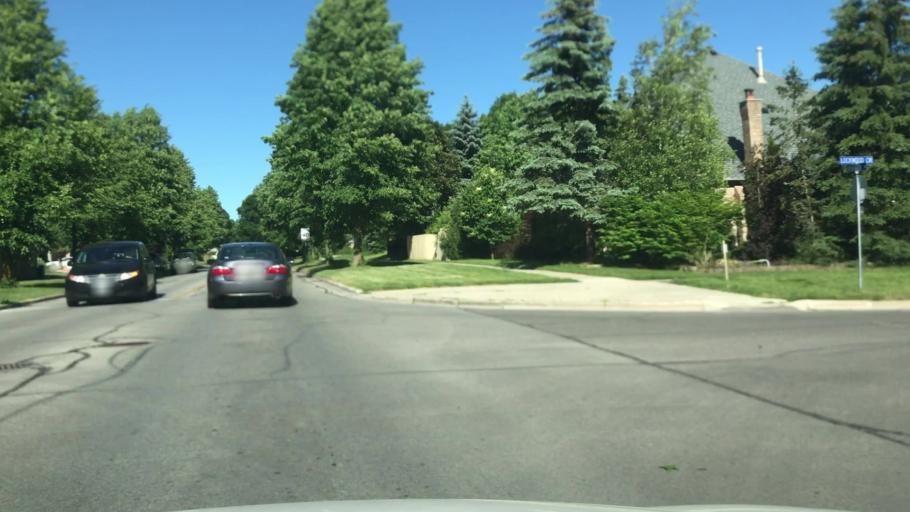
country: CA
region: Ontario
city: Newmarket
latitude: 44.0361
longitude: -79.4304
